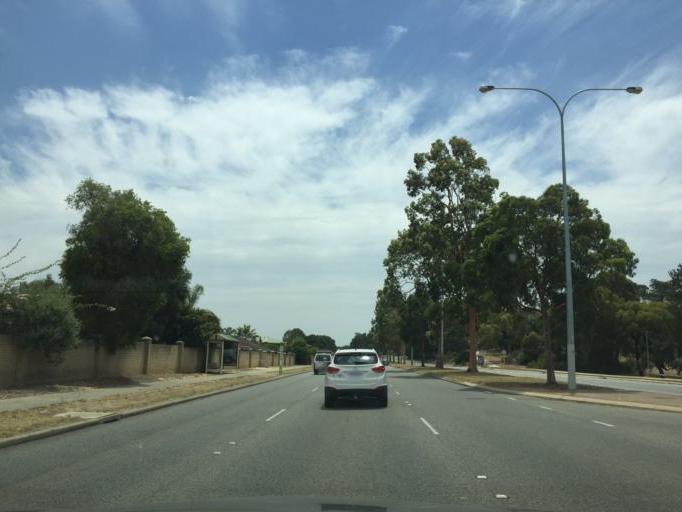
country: AU
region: Western Australia
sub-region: Melville
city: Kardinya
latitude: -32.0671
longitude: 115.8273
